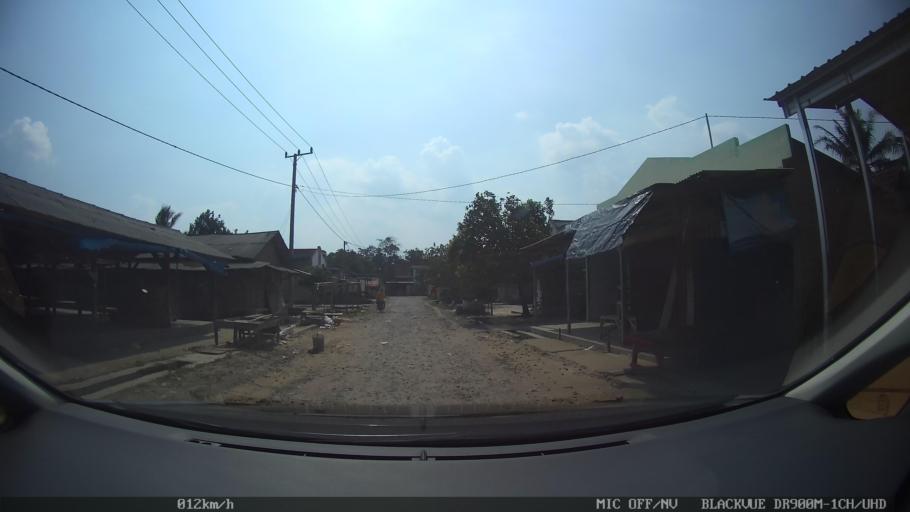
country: ID
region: Lampung
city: Natar
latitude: -5.2945
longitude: 105.2276
